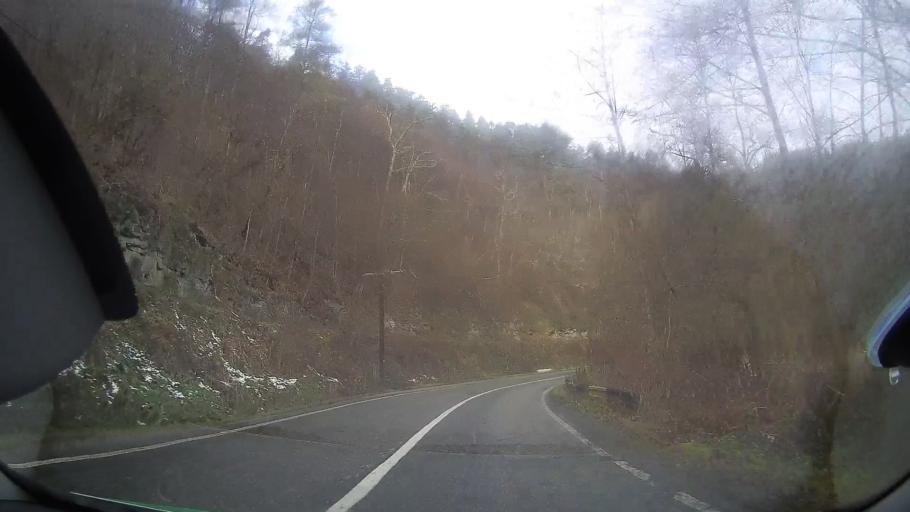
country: RO
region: Alba
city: Salciua de Sus
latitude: 46.4166
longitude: 23.4573
